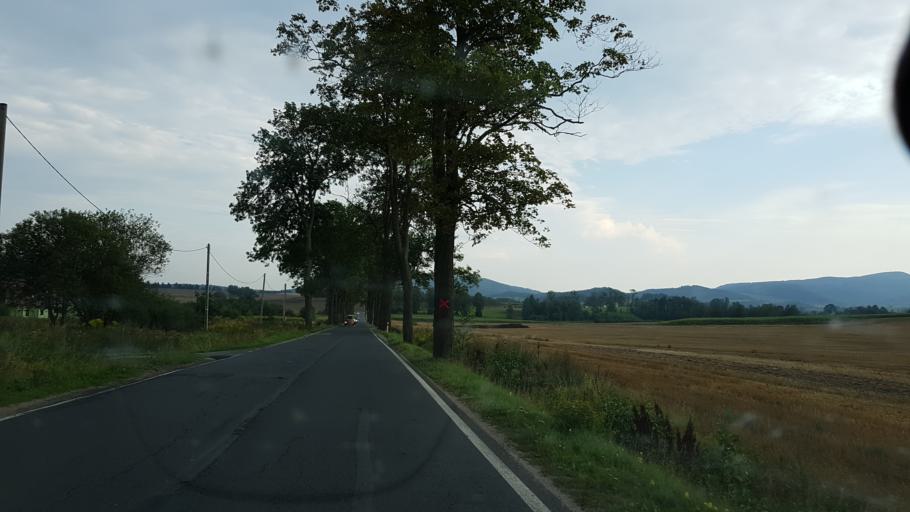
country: PL
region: Lower Silesian Voivodeship
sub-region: Powiat kamiennogorski
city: Marciszow
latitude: 50.8774
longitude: 15.9992
